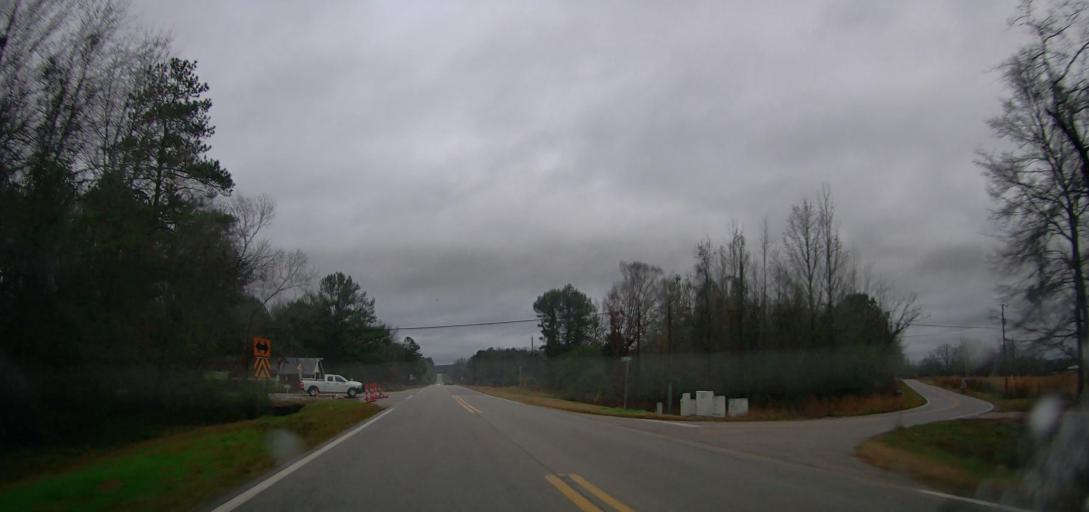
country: US
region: Alabama
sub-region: Bibb County
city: Centreville
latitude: 32.8491
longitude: -86.9616
